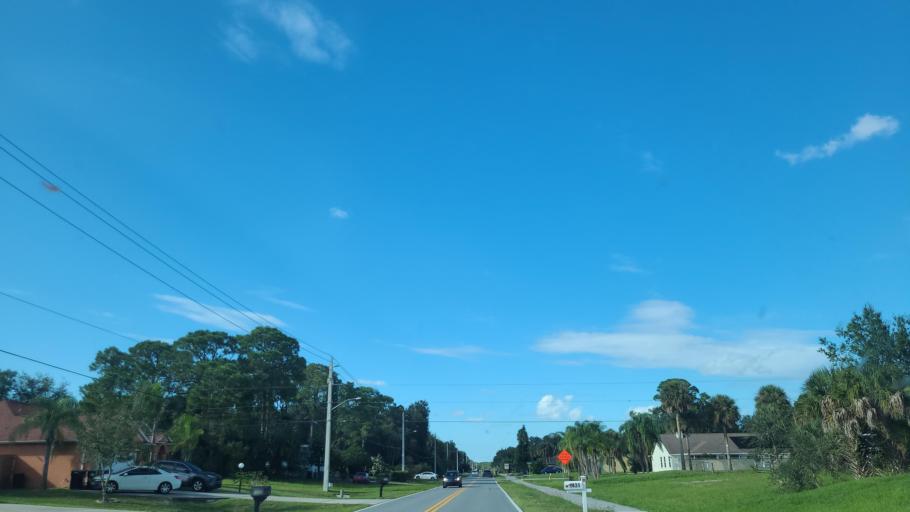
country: US
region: Florida
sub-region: Brevard County
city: Grant-Valkaria
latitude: 27.9615
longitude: -80.6610
